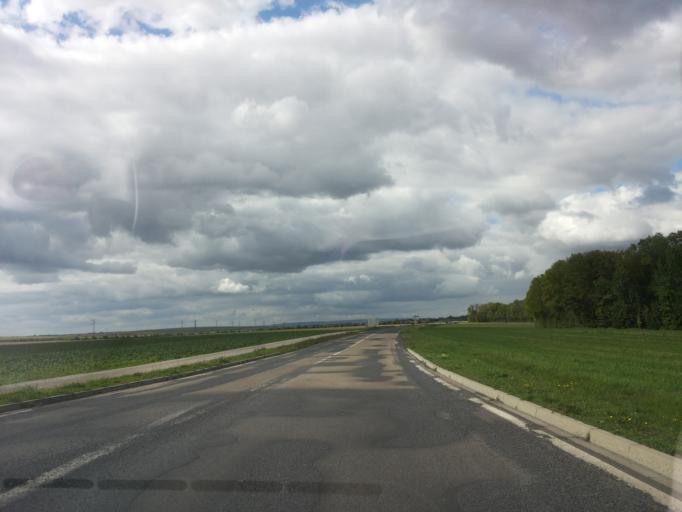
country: FR
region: Champagne-Ardenne
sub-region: Departement de la Marne
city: Courtisols
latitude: 49.0520
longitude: 4.4516
